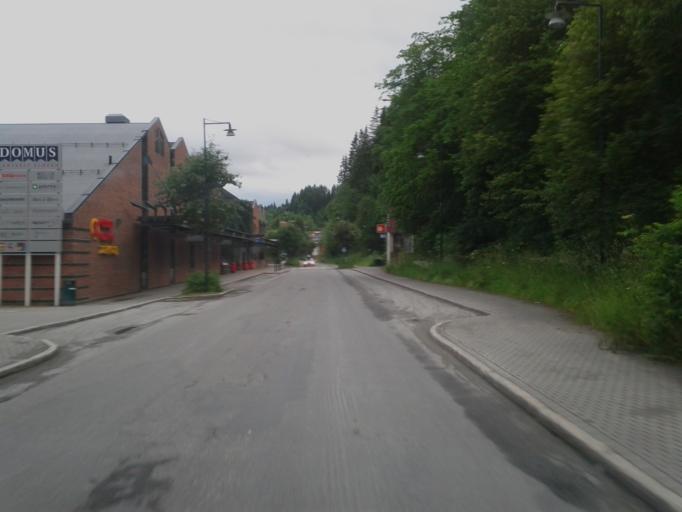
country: NO
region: Sor-Trondelag
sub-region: Midtre Gauldal
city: Storen
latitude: 63.0488
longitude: 10.2832
